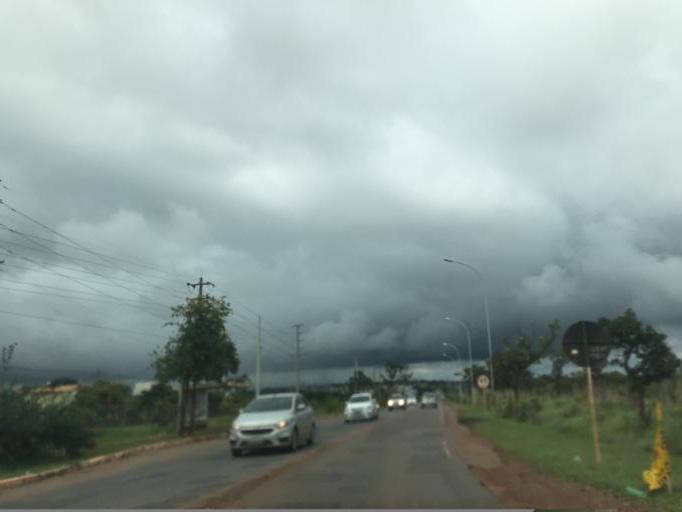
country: BR
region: Federal District
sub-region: Brasilia
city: Brasilia
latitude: -15.8360
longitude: -47.8037
